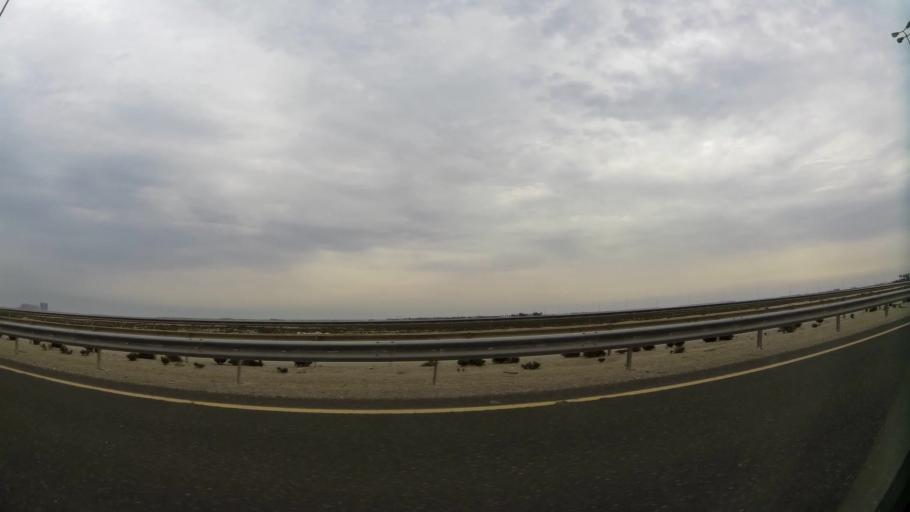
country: BH
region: Central Governorate
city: Dar Kulayb
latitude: 25.8524
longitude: 50.5841
